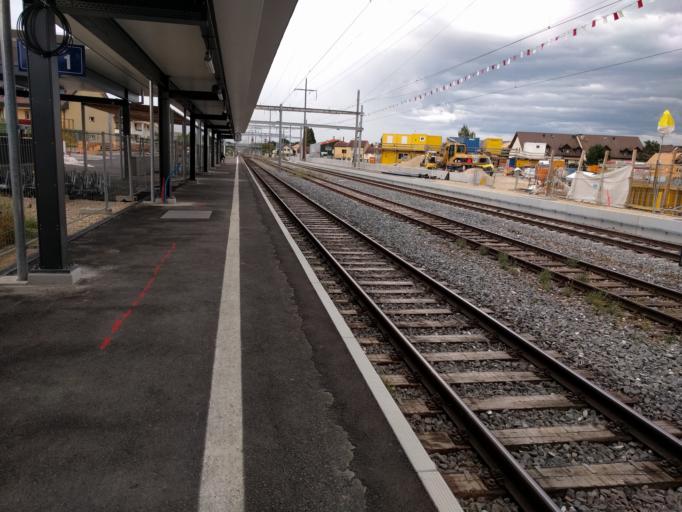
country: CH
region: Vaud
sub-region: Nyon District
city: Gland
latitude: 46.4202
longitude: 6.2695
